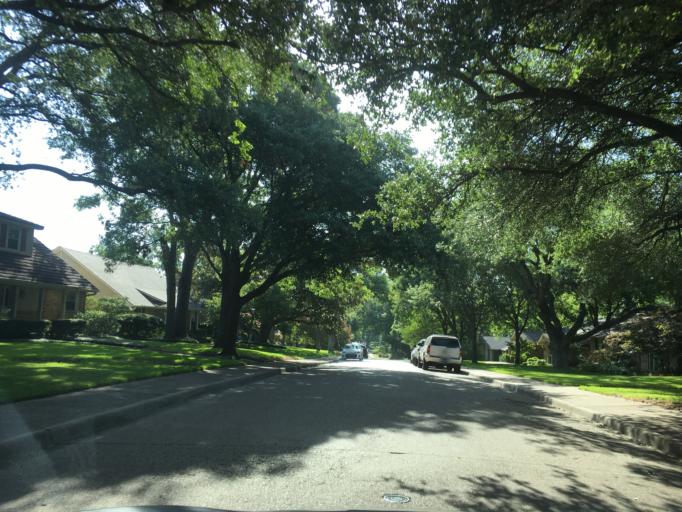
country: US
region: Texas
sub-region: Dallas County
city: Richardson
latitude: 32.8839
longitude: -96.7224
